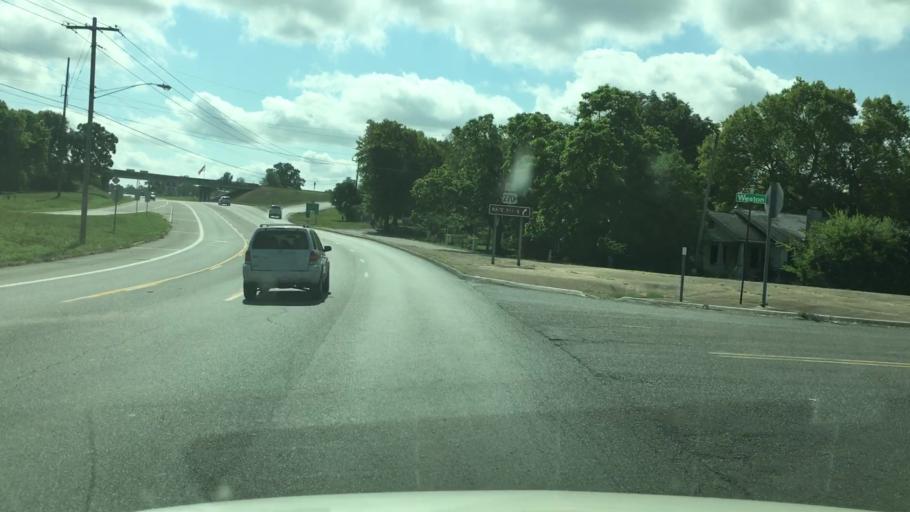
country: US
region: Arkansas
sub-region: Garland County
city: Piney
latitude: 34.4929
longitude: -93.1150
